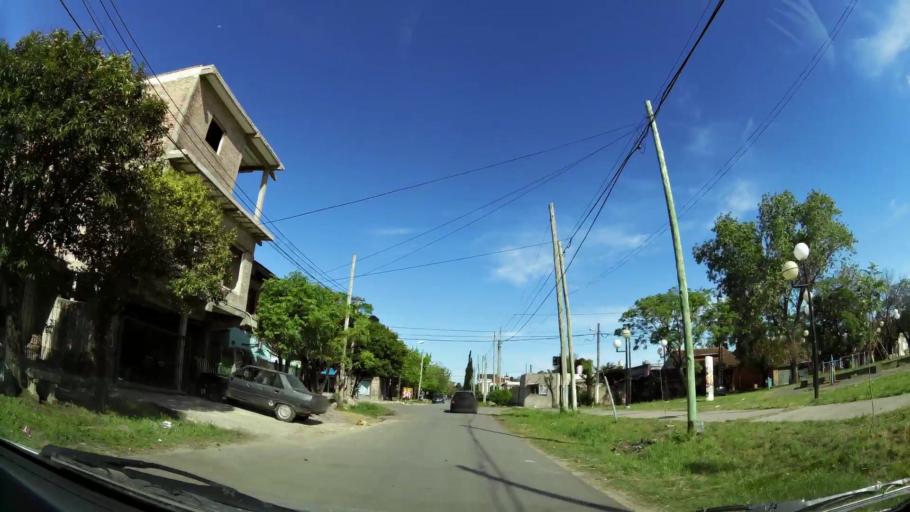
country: AR
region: Buenos Aires
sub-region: Partido de Quilmes
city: Quilmes
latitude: -34.7962
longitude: -58.2398
